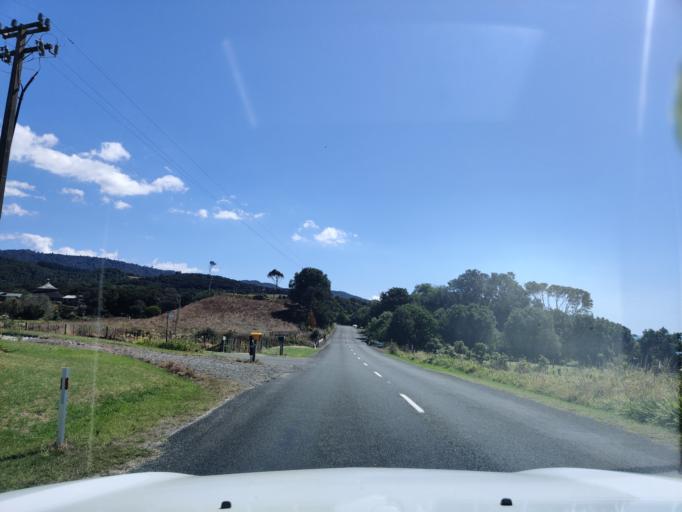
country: NZ
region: Waikato
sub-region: Thames-Coromandel District
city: Thames
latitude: -37.0440
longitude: 175.2973
